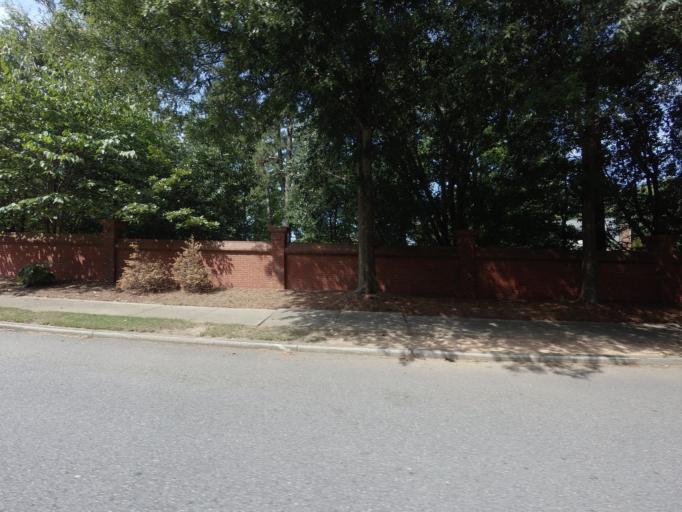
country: US
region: Georgia
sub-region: Fulton County
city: Johns Creek
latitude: 34.0331
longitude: -84.2345
